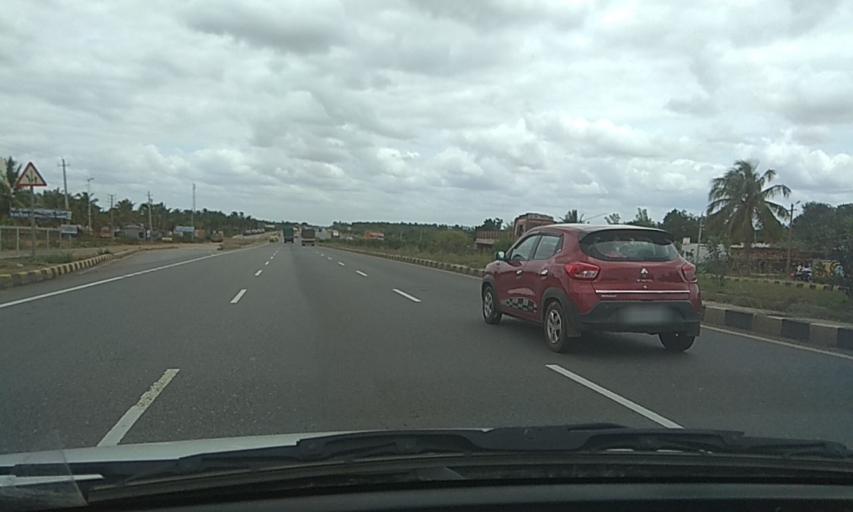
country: IN
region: Karnataka
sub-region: Tumkur
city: Sira
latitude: 13.8234
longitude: 76.7743
